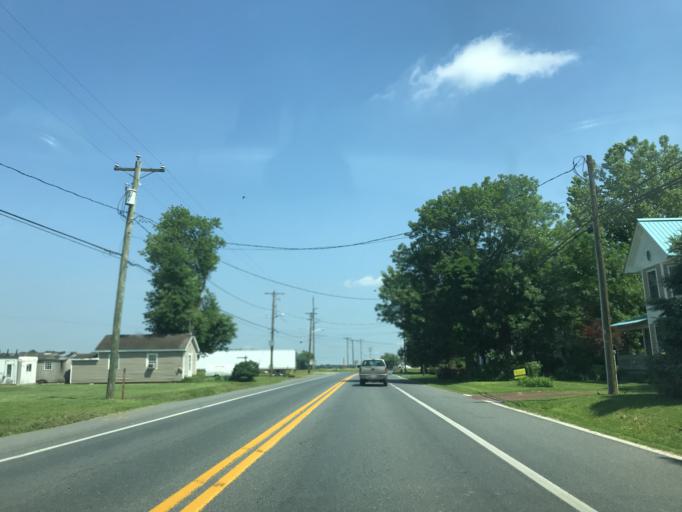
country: US
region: Maryland
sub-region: Dorchester County
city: Hurlock
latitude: 38.5774
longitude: -75.8384
